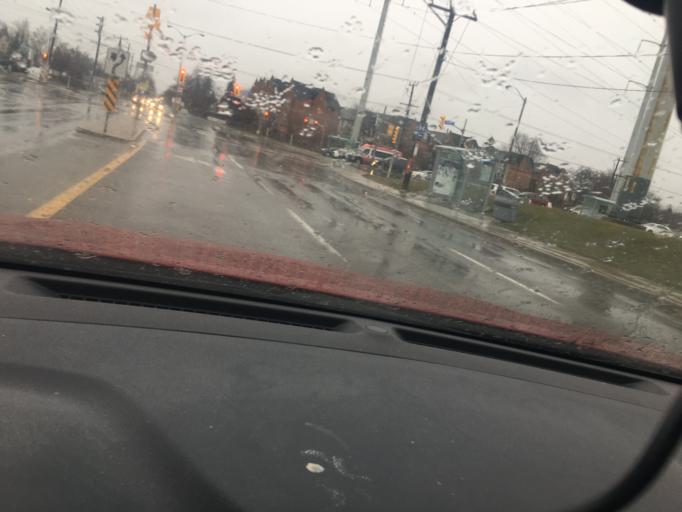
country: CA
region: Ontario
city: Scarborough
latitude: 43.7541
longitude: -79.2556
